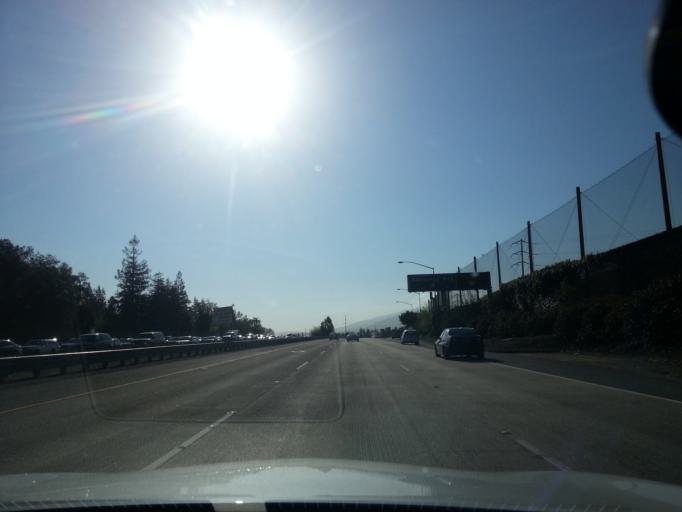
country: US
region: California
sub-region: Santa Clara County
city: Saratoga
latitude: 37.2800
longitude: -122.0117
